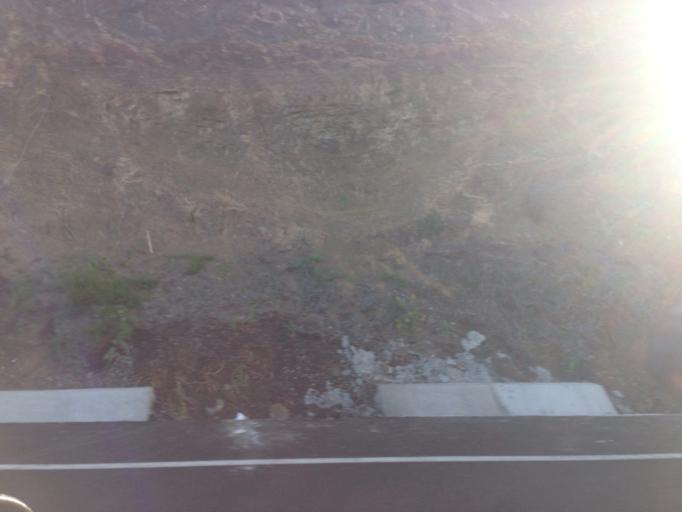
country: MX
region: Baja California
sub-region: Playas de Rosarito
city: Santa Anita
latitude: 32.1432
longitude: -116.8909
